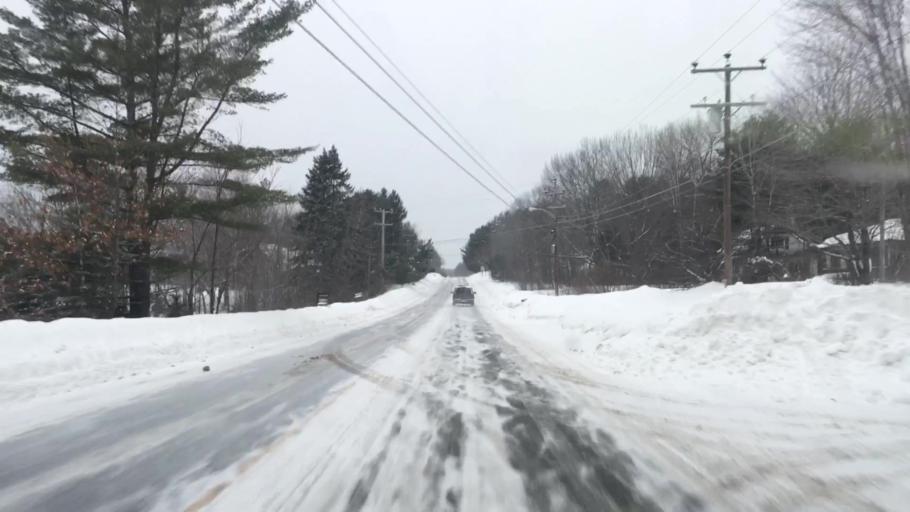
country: US
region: Maine
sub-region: Penobscot County
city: Medway
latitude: 45.5959
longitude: -68.4945
